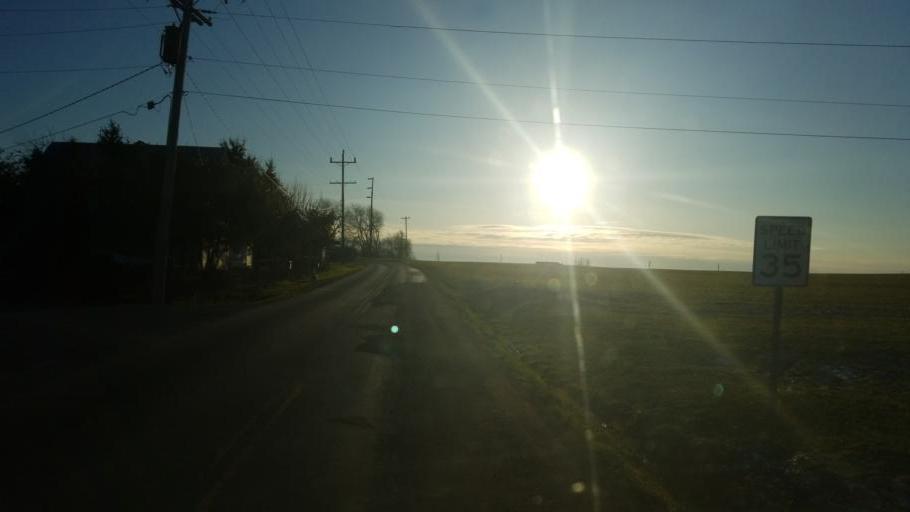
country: US
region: Ohio
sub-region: Highland County
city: Greenfield
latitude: 39.2604
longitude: -83.4482
